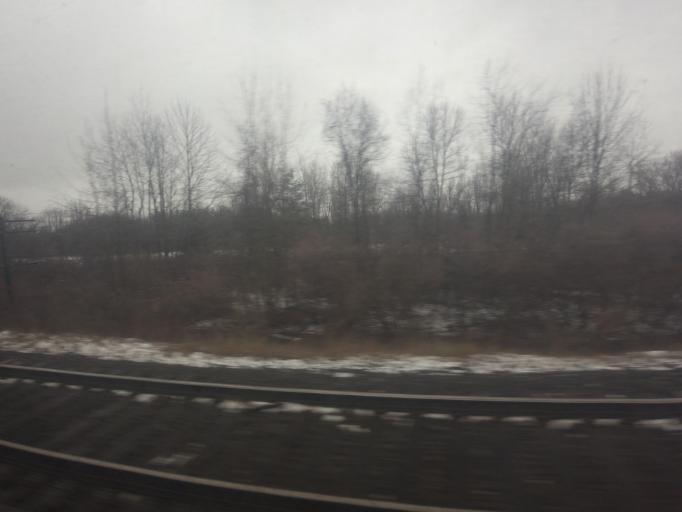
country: CA
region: Ontario
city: Quinte West
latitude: 44.0686
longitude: -77.6643
